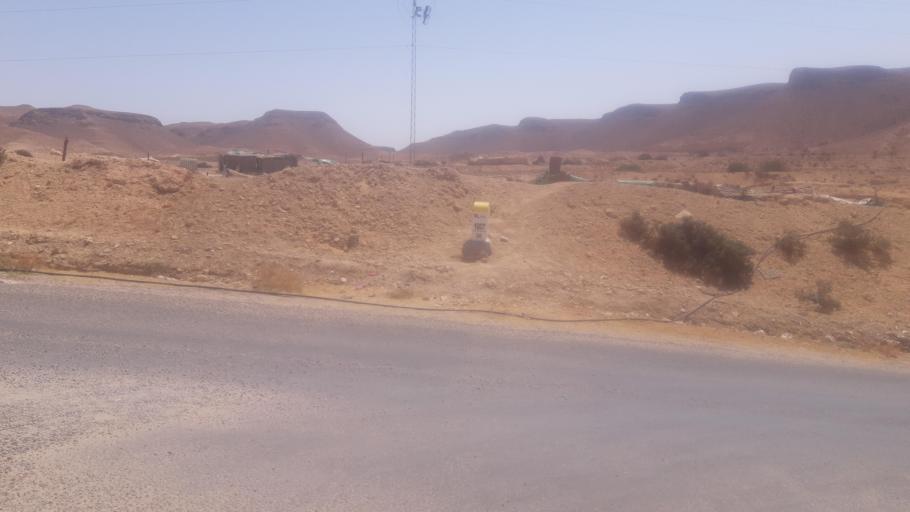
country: TN
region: Tataouine
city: Tataouine
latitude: 32.8555
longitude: 10.2911
